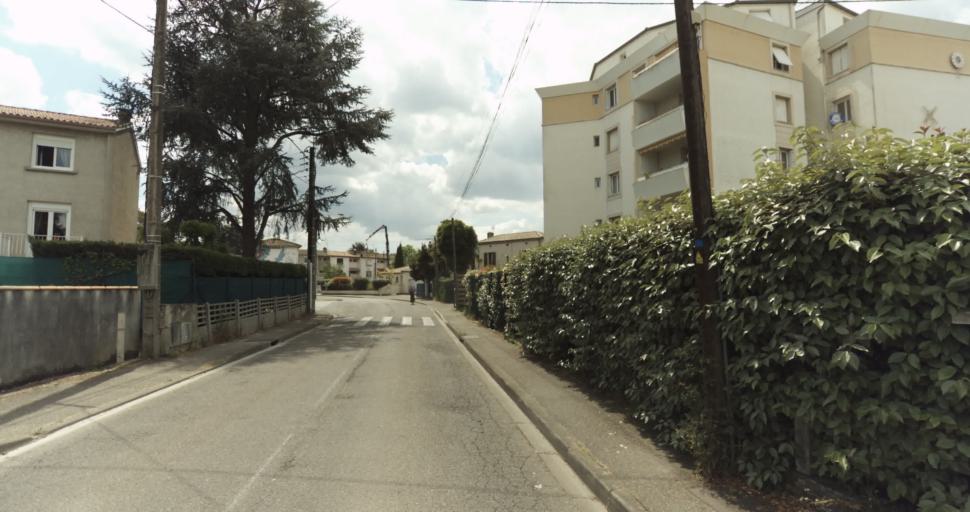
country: FR
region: Aquitaine
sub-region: Departement du Lot-et-Garonne
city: Agen
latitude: 44.1931
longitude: 0.6247
